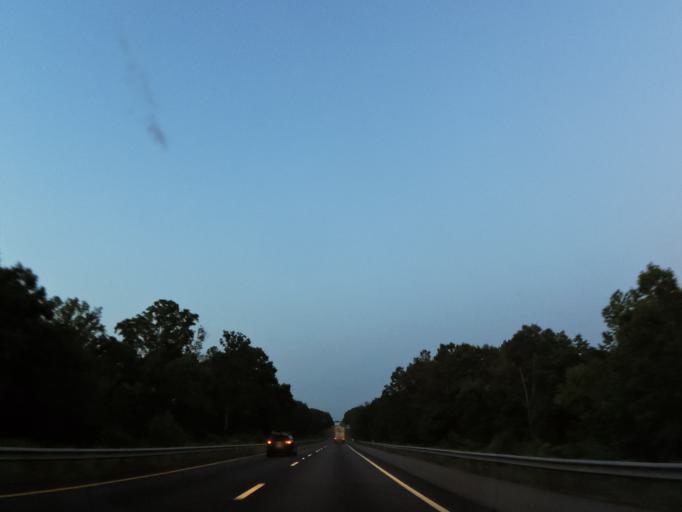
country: US
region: Tennessee
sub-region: Bradley County
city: Cleveland
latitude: 35.1422
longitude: -84.9845
